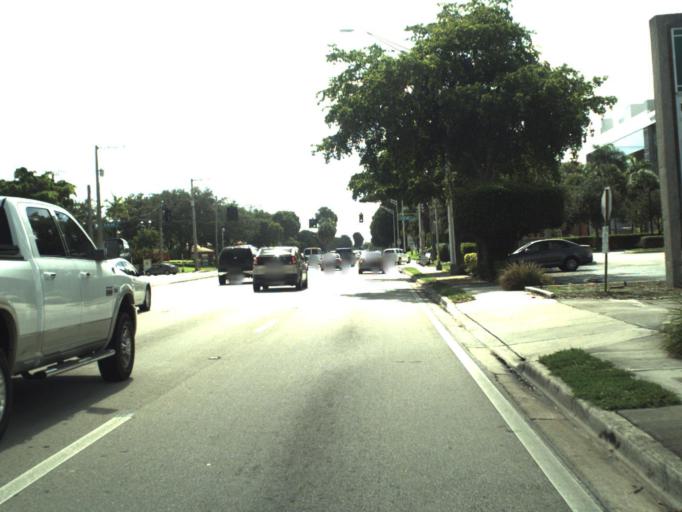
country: US
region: Florida
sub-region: Broward County
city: Carver Ranches
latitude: 26.0328
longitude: -80.1891
